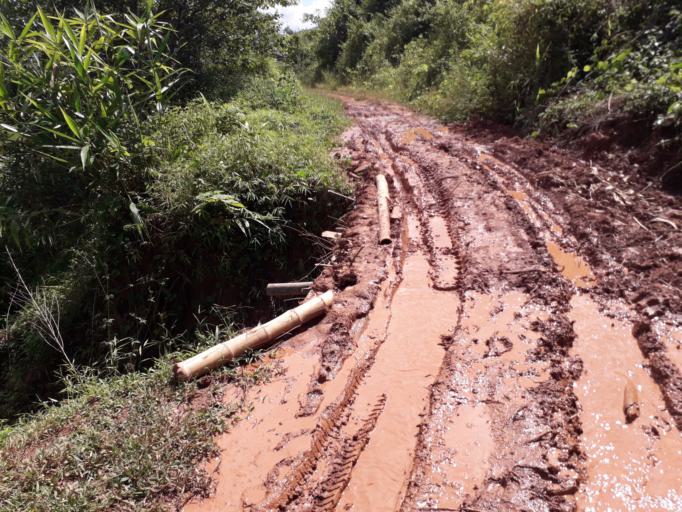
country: CN
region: Yunnan
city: Menglie
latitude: 22.0948
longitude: 101.7370
